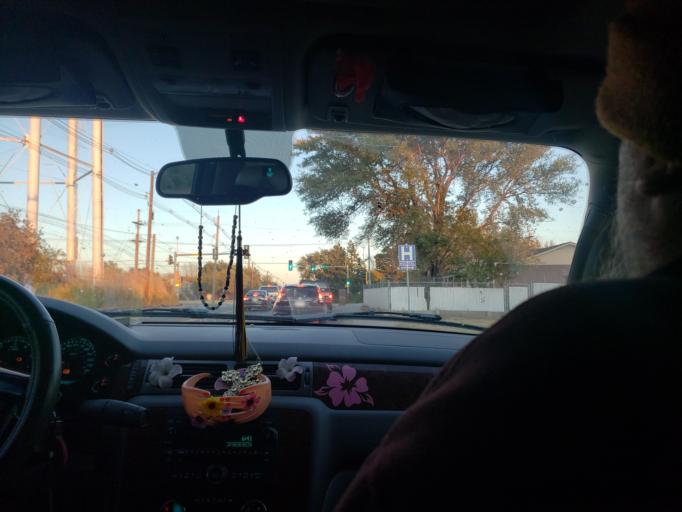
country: US
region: Kansas
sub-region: Finney County
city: Garden City
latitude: 37.9894
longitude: -100.8666
